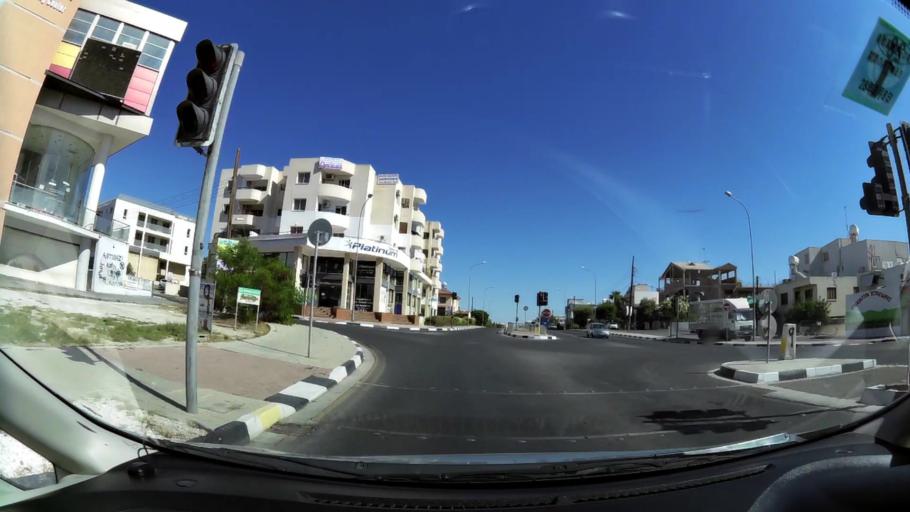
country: CY
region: Larnaka
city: Larnaca
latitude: 34.9325
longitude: 33.6151
